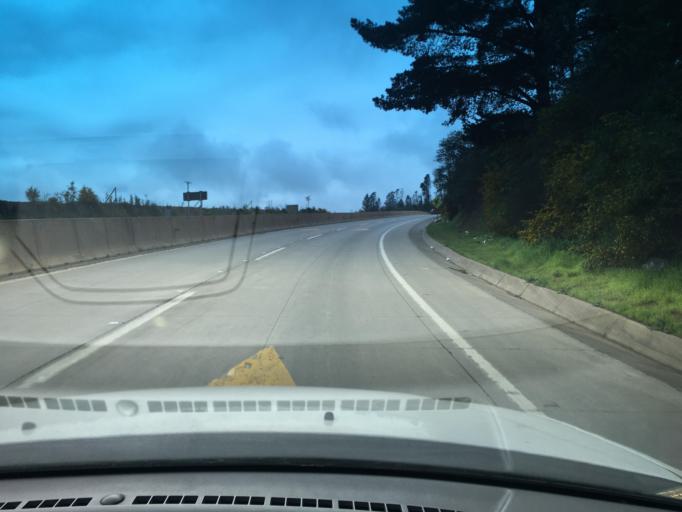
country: CL
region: Valparaiso
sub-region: Provincia de Valparaiso
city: Valparaiso
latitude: -33.0914
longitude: -71.6091
